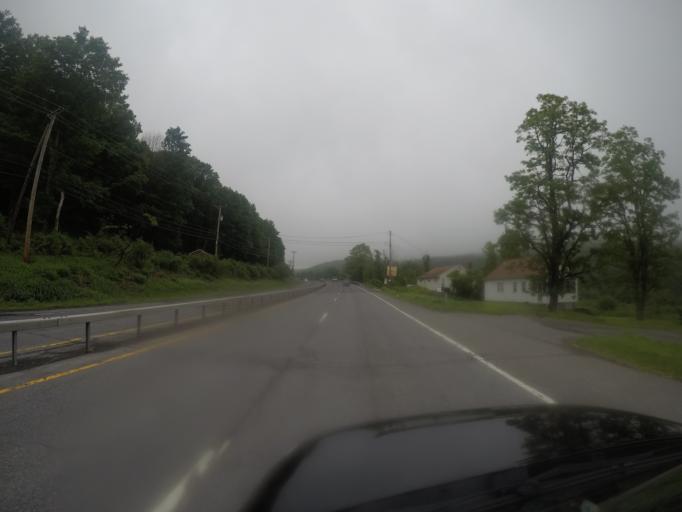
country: US
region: New York
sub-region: Ulster County
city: Hurley
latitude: 41.9557
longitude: -74.0494
